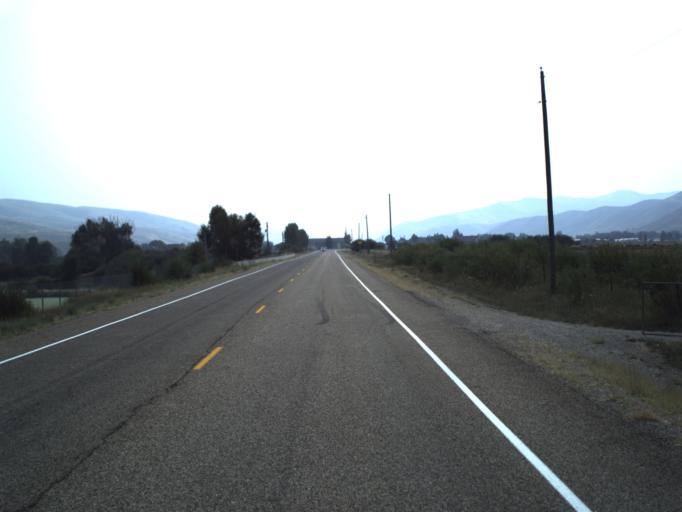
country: US
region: Utah
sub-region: Summit County
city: Coalville
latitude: 41.0300
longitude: -111.5101
